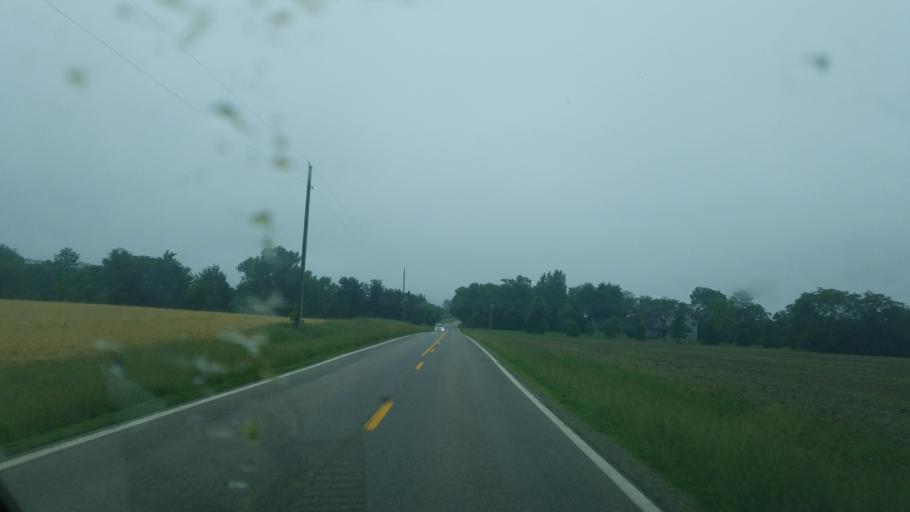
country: US
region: Ohio
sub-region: Delaware County
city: Ashley
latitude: 40.4739
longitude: -82.9633
